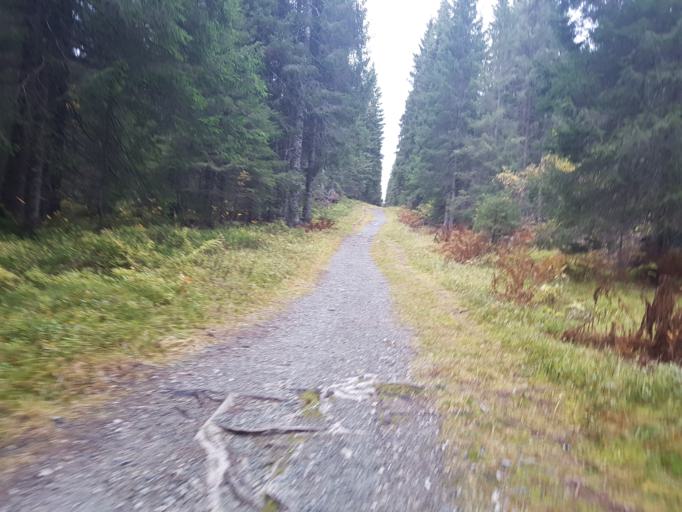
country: NO
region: Sor-Trondelag
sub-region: Melhus
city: Melhus
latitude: 63.3815
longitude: 10.2536
